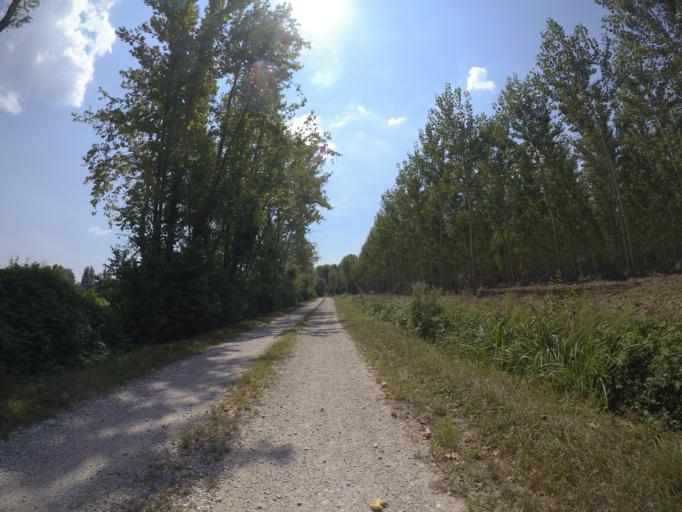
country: IT
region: Friuli Venezia Giulia
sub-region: Provincia di Udine
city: Bertiolo
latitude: 45.9127
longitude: 13.0611
